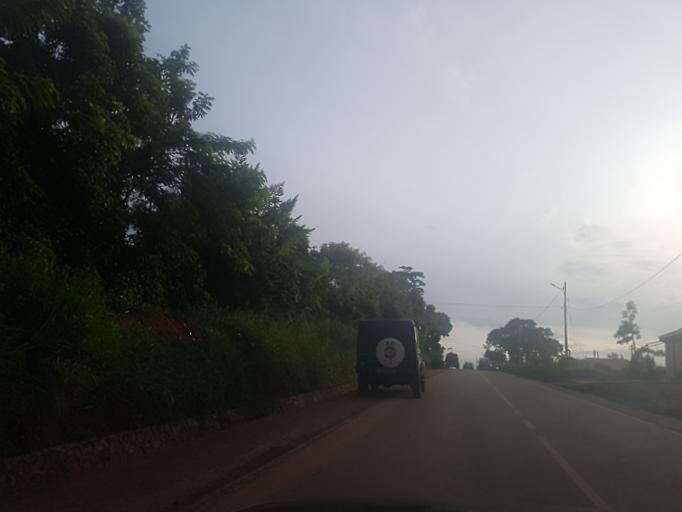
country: UG
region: Central Region
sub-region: Wakiso District
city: Bweyogerere
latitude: 0.3968
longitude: 32.6699
